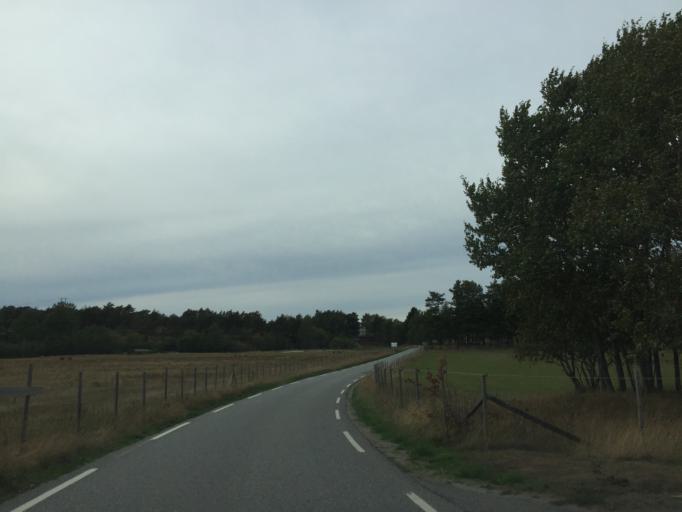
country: NO
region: Ostfold
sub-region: Hvaler
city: Skjaerhalden
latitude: 59.0395
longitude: 11.0367
